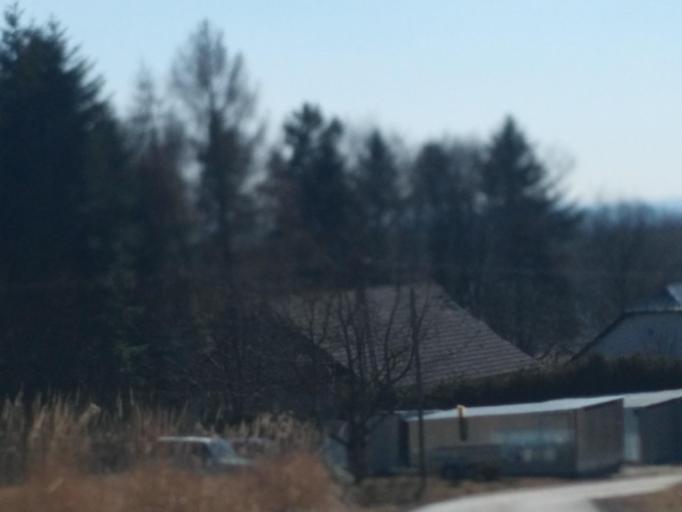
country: PL
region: Subcarpathian Voivodeship
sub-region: Powiat ropczycko-sedziszowski
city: Zagorzyce
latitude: 49.9660
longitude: 21.7236
